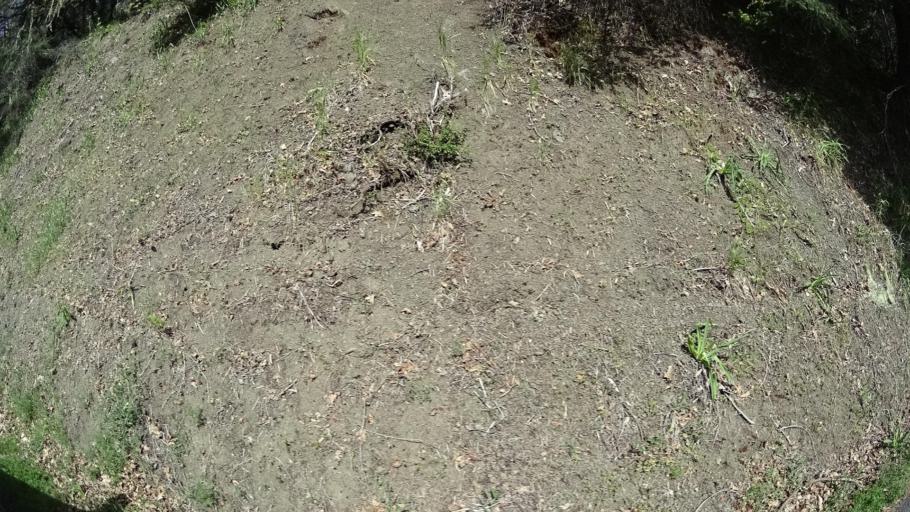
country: US
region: California
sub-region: Humboldt County
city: Redway
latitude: 40.3531
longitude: -123.7185
